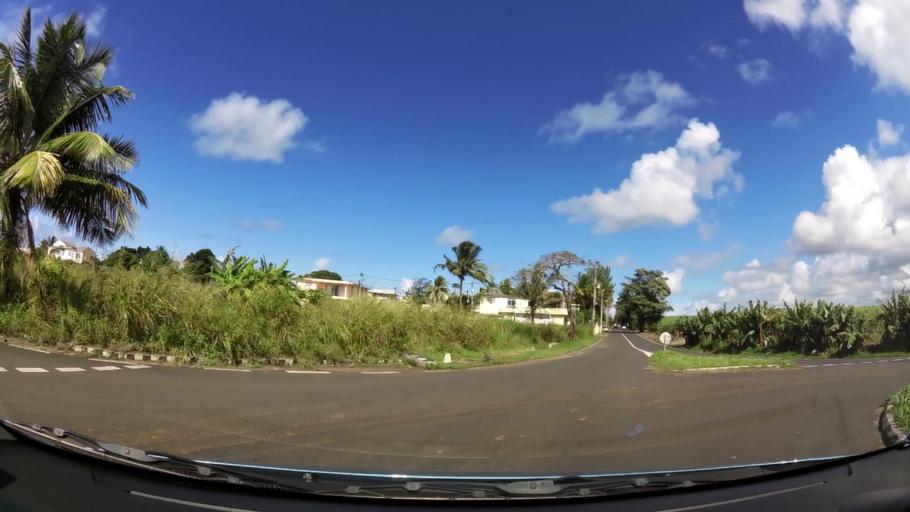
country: MU
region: Grand Port
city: Plaine Magnien
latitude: -20.4255
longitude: 57.6694
